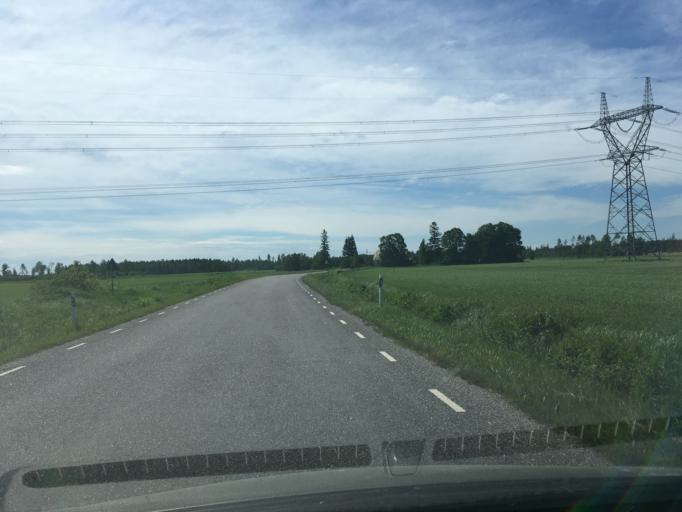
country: EE
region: Paernumaa
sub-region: Audru vald
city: Audru
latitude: 58.4338
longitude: 24.4000
